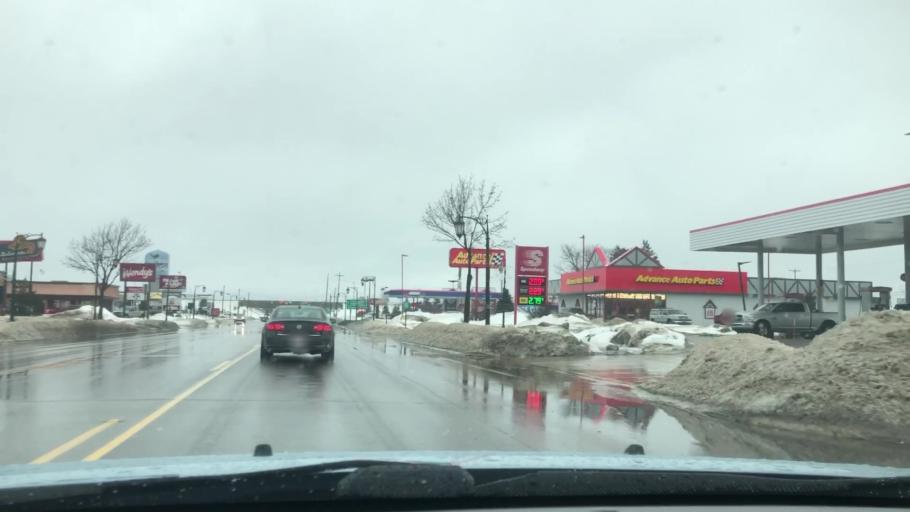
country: US
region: Michigan
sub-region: Otsego County
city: Gaylord
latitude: 45.0274
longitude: -84.6833
